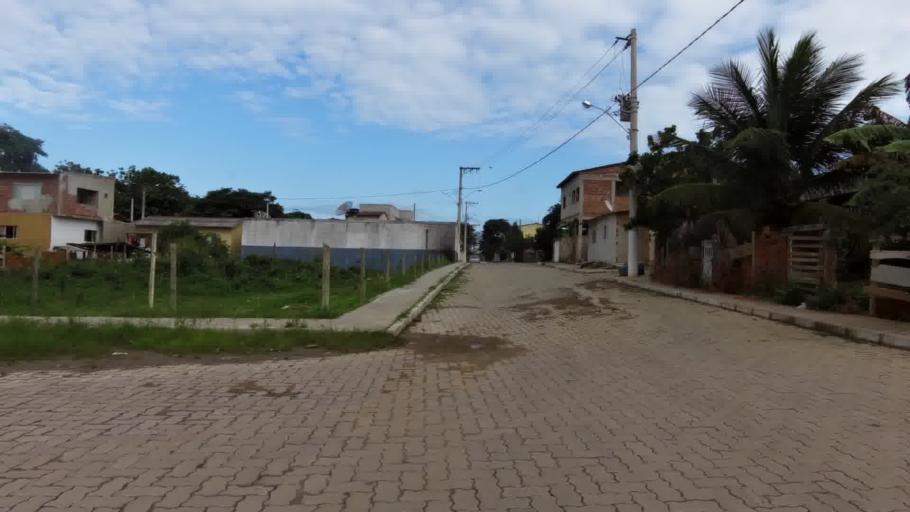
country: BR
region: Espirito Santo
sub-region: Piuma
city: Piuma
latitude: -20.7913
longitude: -40.6389
